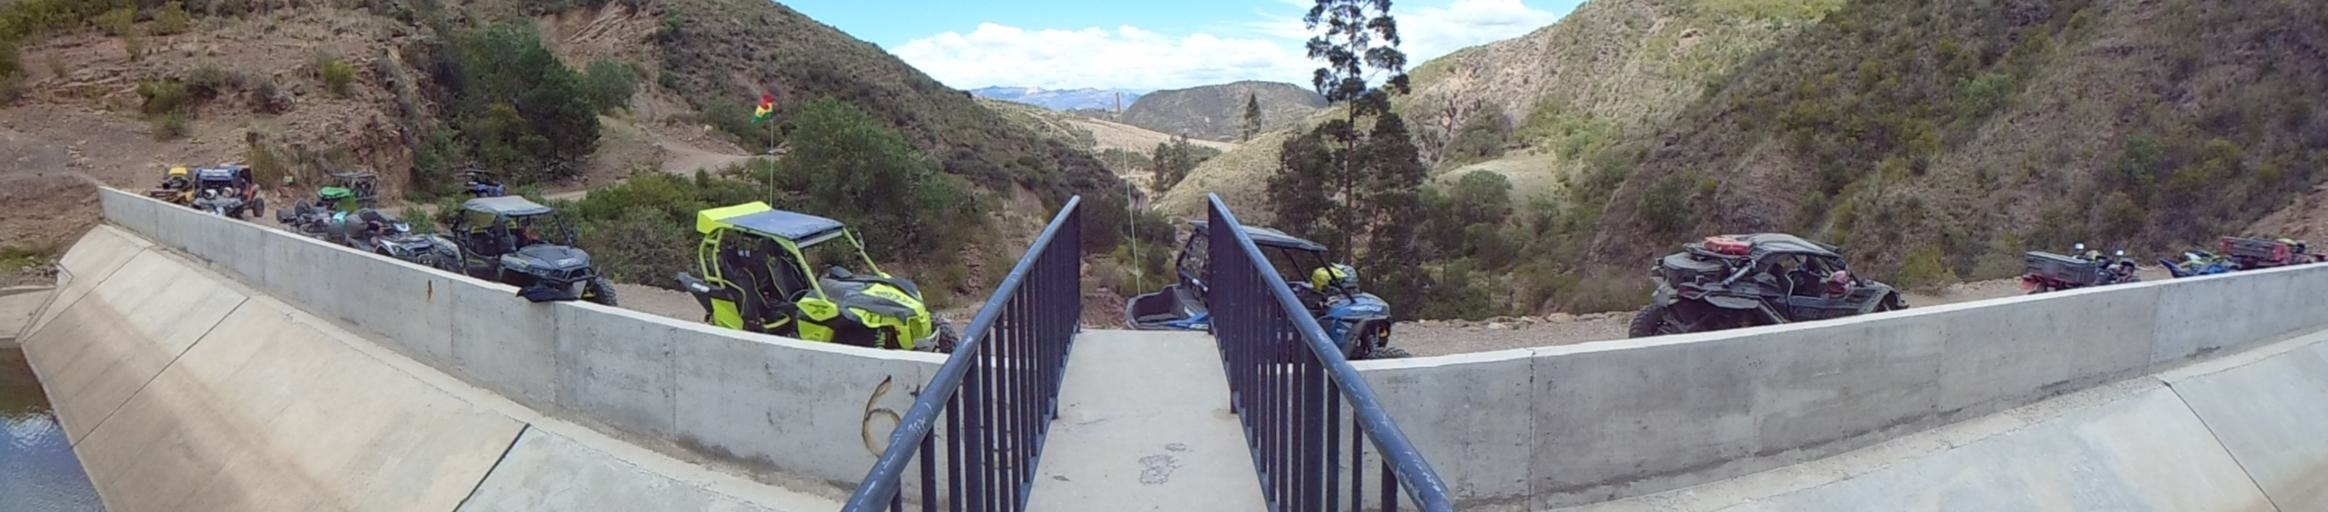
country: BO
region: Cochabamba
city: Capinota
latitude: -17.6828
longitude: -66.1672
